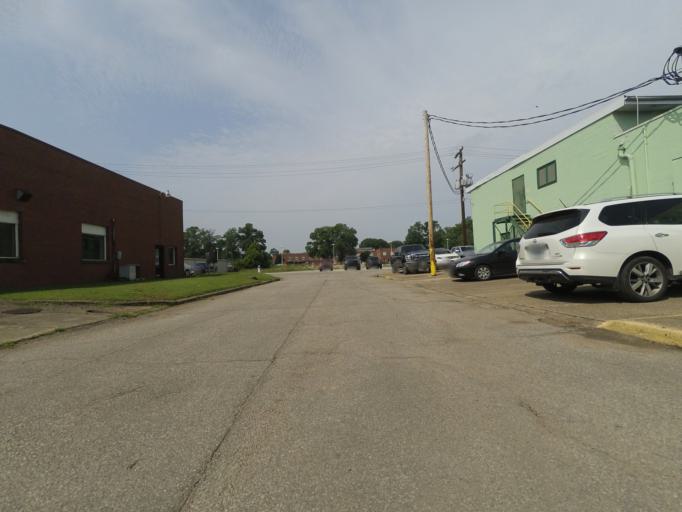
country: US
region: West Virginia
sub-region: Cabell County
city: Huntington
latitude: 38.4118
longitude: -82.4651
